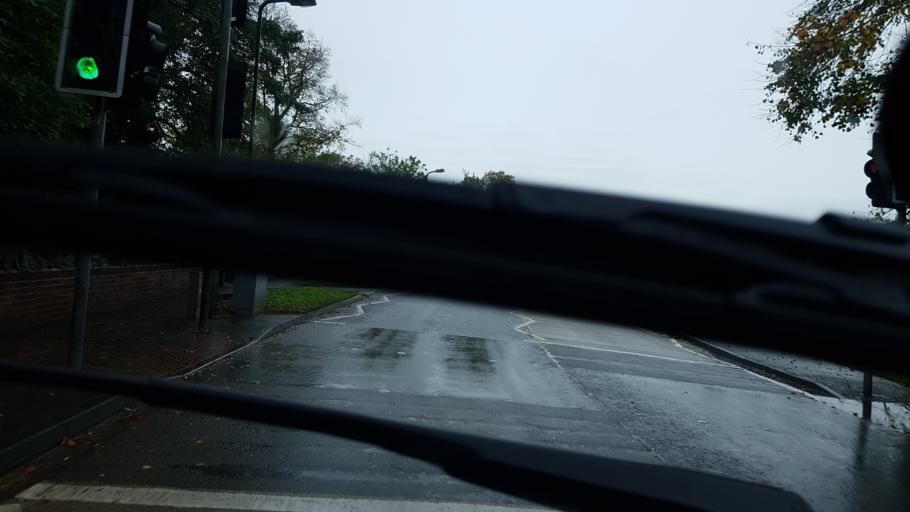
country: GB
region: England
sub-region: Worcestershire
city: Upton upon Severn
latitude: 52.0601
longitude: -2.2186
